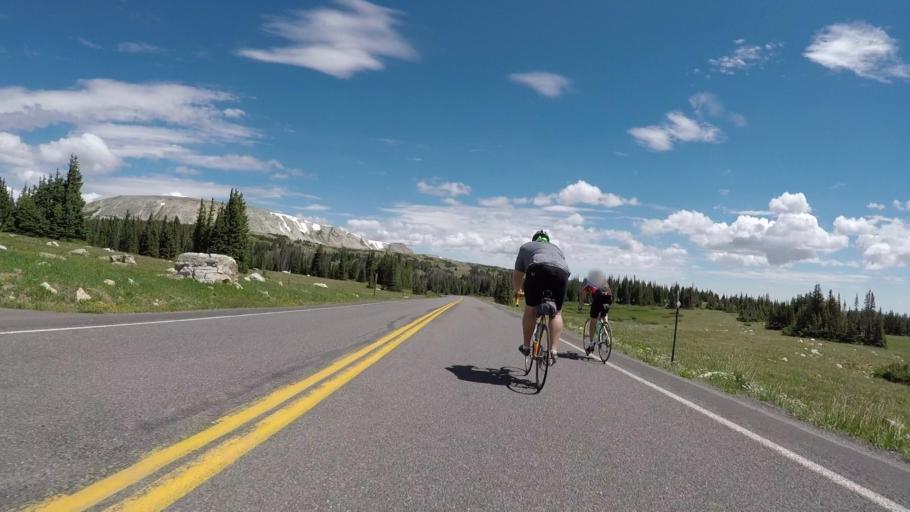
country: US
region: Wyoming
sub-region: Carbon County
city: Saratoga
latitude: 41.3471
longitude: -106.2902
